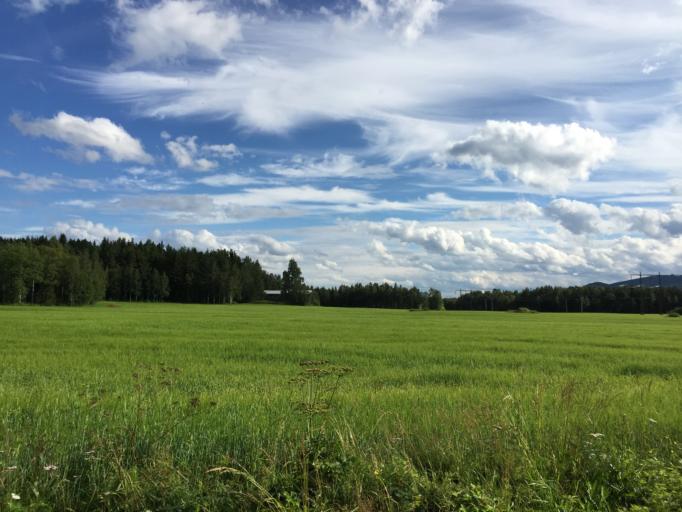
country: SE
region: Gaevleborg
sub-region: Ljusdals Kommun
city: Jaervsoe
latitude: 61.7630
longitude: 16.1788
